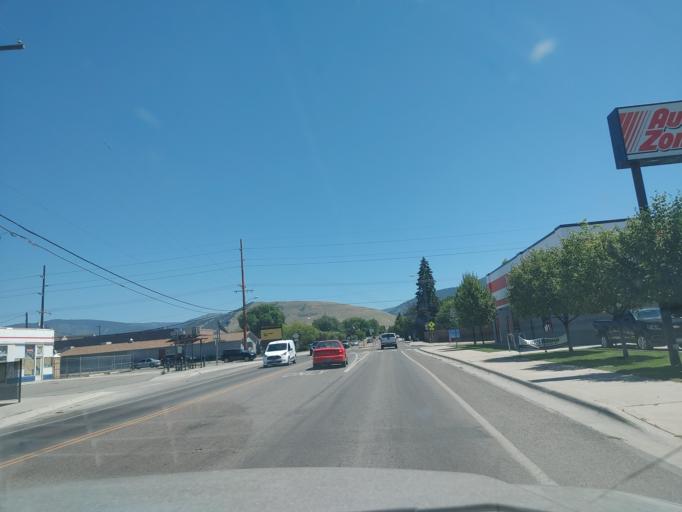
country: US
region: Montana
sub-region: Missoula County
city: Orchard Homes
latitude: 46.8670
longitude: -114.0234
